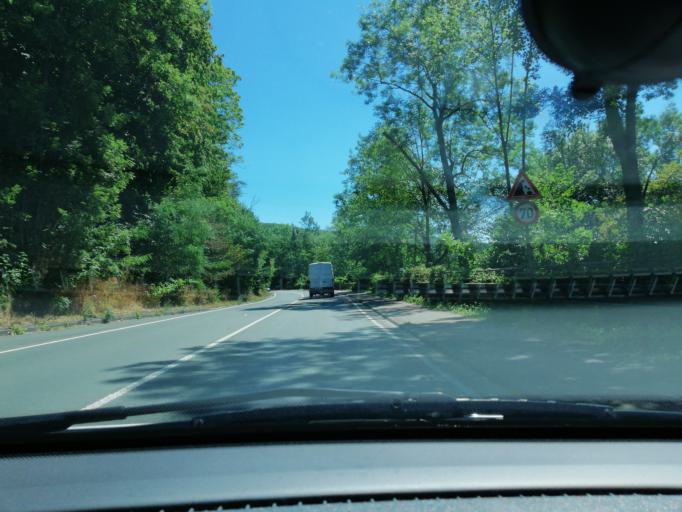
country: DE
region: North Rhine-Westphalia
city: Witten
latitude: 51.4269
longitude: 7.3468
